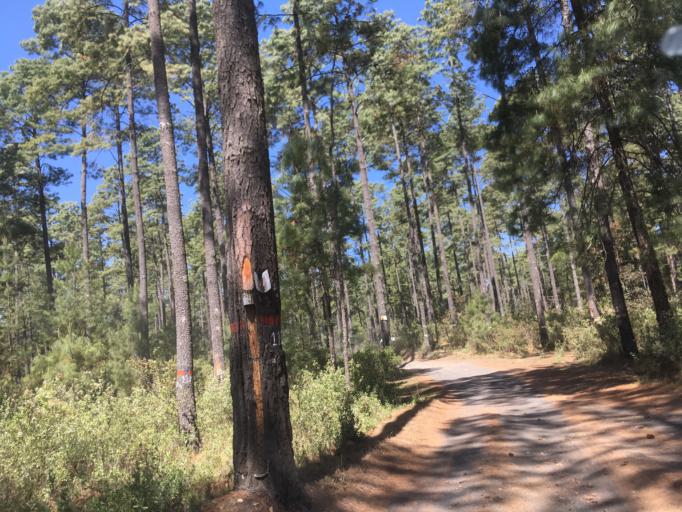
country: MX
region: Michoacan
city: Nuevo San Juan Parangaricutiro
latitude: 19.4597
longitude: -102.2081
